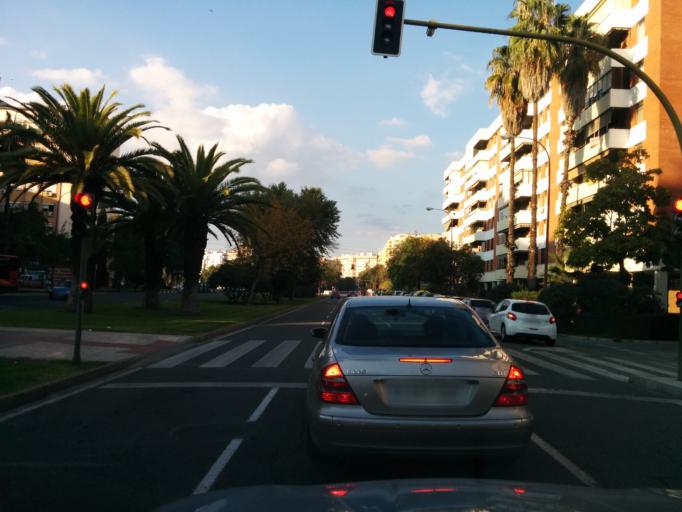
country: ES
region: Andalusia
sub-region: Provincia de Sevilla
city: Sevilla
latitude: 37.3886
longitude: -5.9202
